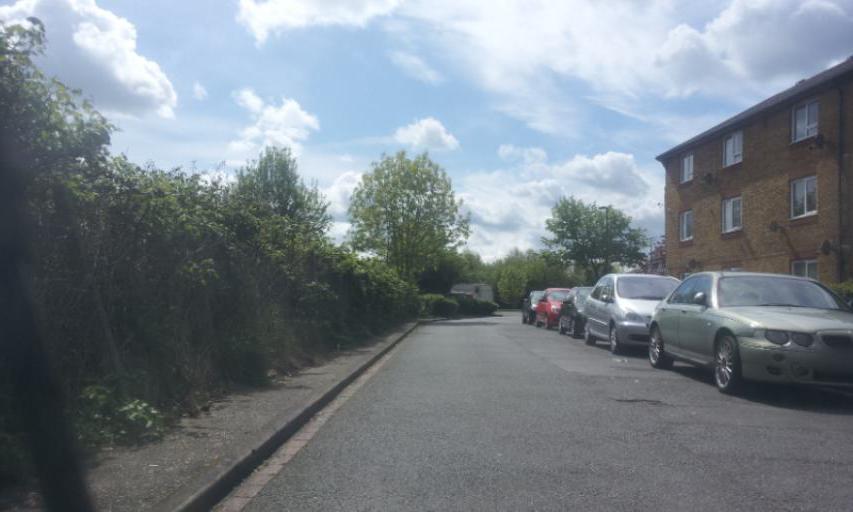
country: GB
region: England
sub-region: Greater London
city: Beckenham
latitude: 51.4274
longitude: -0.0329
